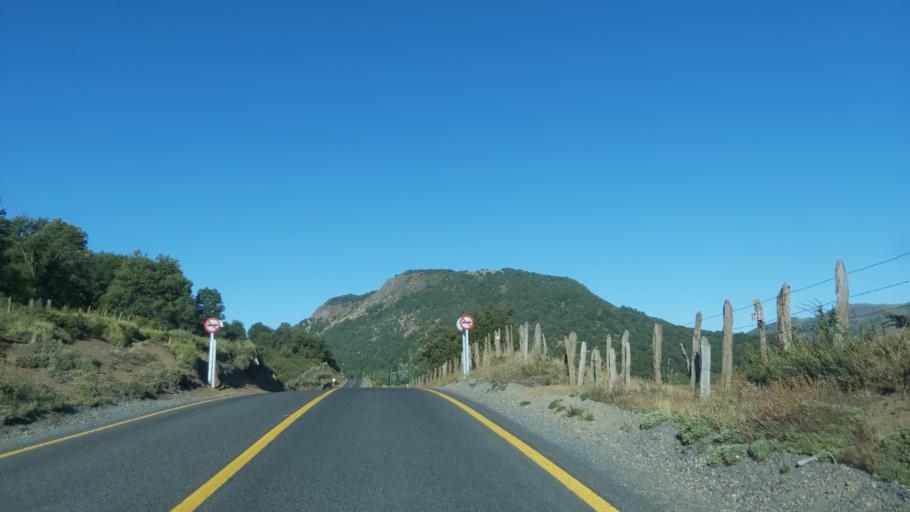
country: AR
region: Neuquen
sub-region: Departamento de Loncopue
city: Loncopue
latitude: -38.4446
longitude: -71.3472
